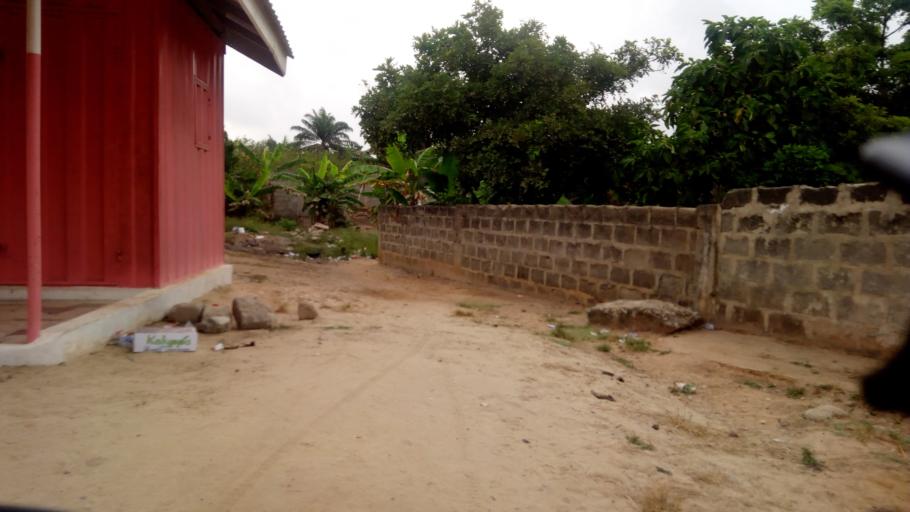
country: GH
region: Central
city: Cape Coast
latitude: 5.1164
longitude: -1.2687
